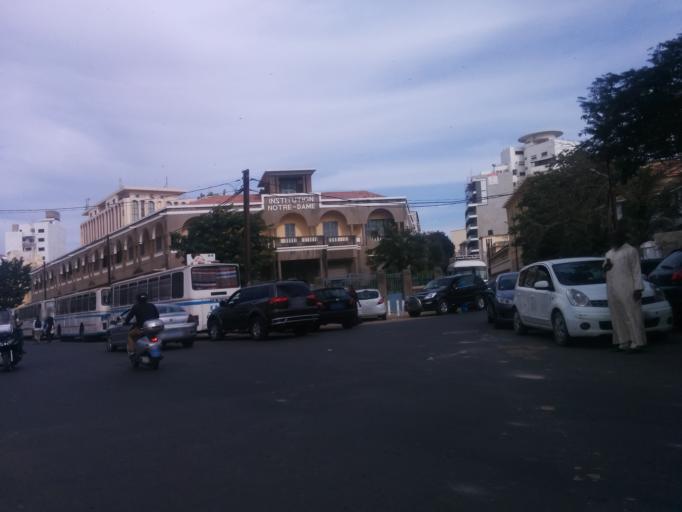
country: SN
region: Dakar
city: Dakar
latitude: 14.6643
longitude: -17.4402
